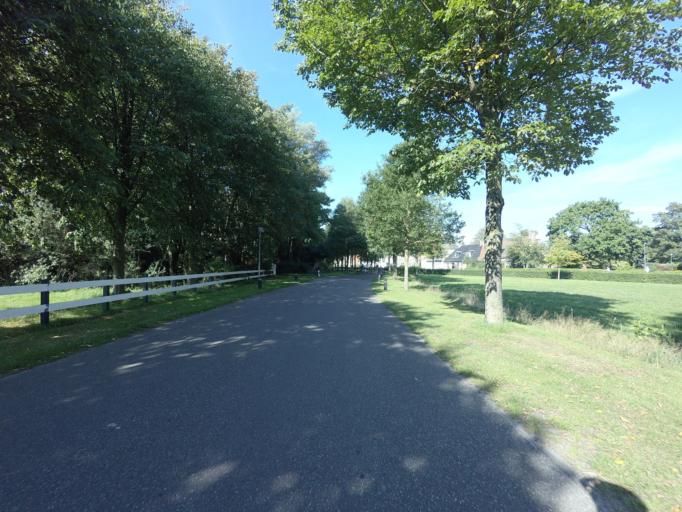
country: NL
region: Friesland
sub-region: Gemeente Schiermonnikoog
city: Schiermonnikoog
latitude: 53.4805
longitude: 6.1677
